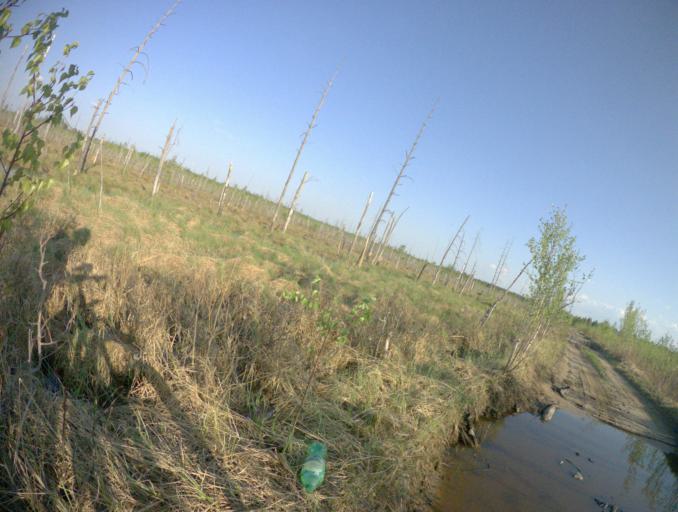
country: RU
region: Vladimir
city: Vyazniki
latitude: 56.3849
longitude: 42.1726
